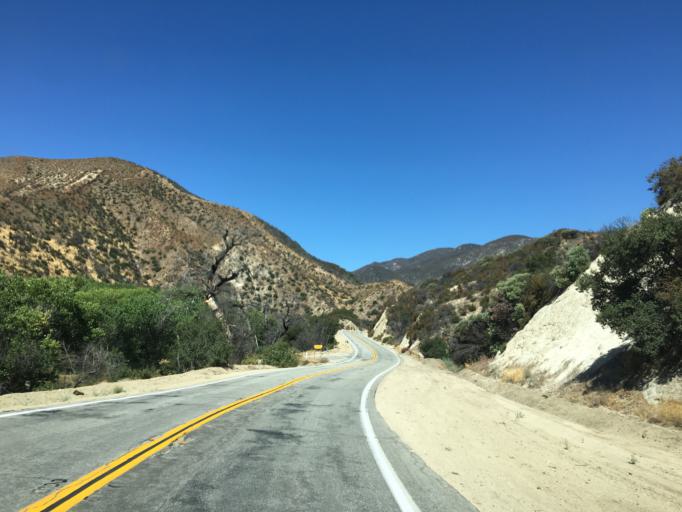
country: US
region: California
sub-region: Los Angeles County
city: Green Valley
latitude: 34.6403
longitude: -118.5016
